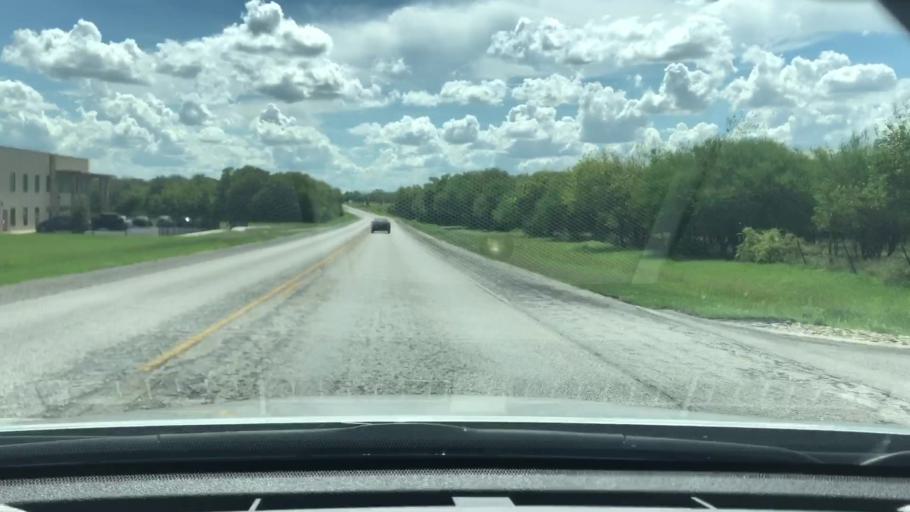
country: US
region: Texas
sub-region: Bexar County
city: Converse
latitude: 29.5256
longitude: -98.3104
